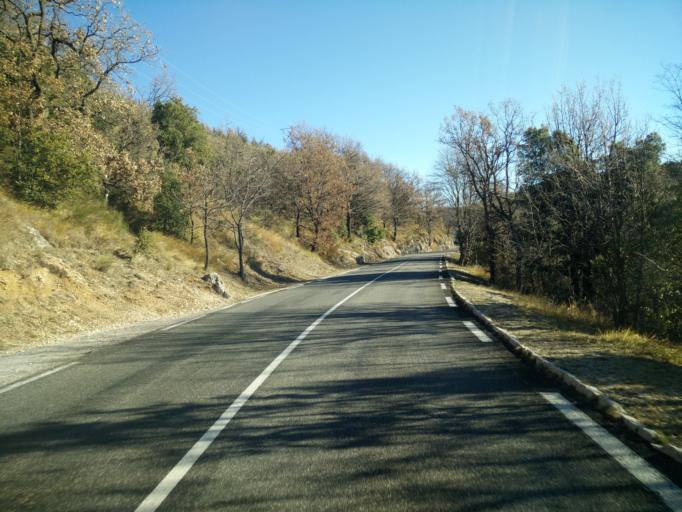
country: FR
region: Provence-Alpes-Cote d'Azur
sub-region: Departement des Alpes-Maritimes
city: Saint-Vallier-de-Thiey
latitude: 43.7210
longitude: 6.8239
